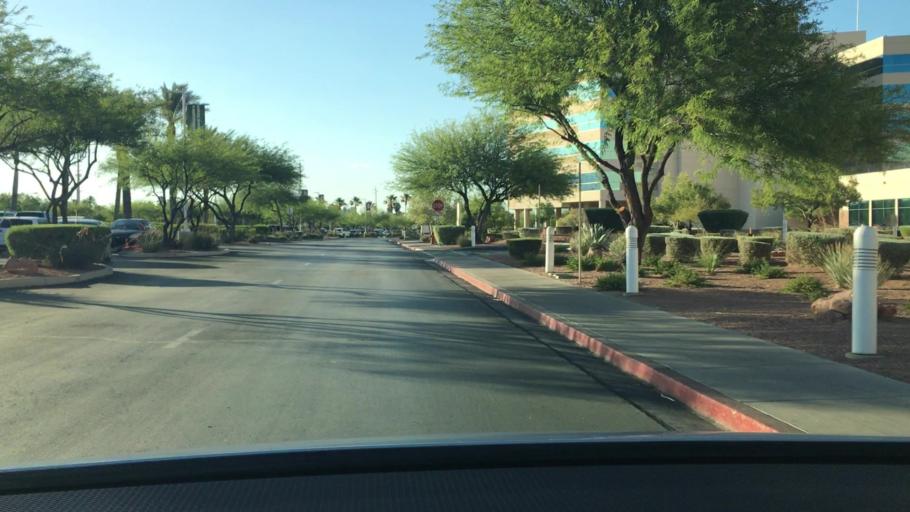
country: US
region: Nevada
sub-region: Clark County
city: Spring Valley
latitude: 36.2153
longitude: -115.2498
